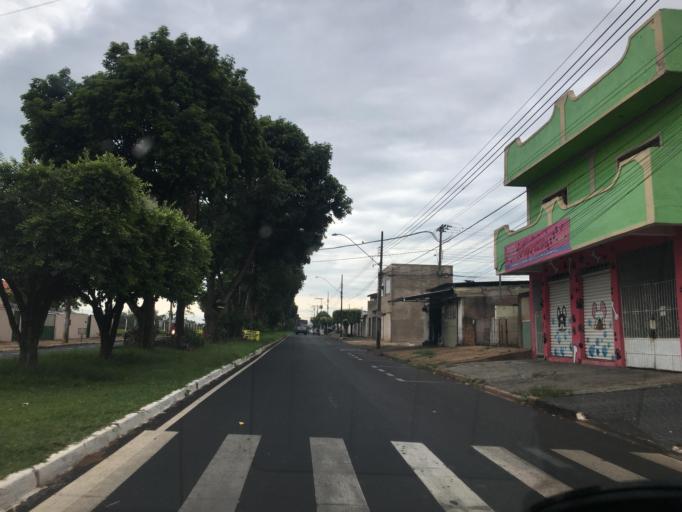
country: BR
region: Minas Gerais
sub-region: Uberlandia
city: Uberlandia
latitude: -18.9282
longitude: -48.3134
